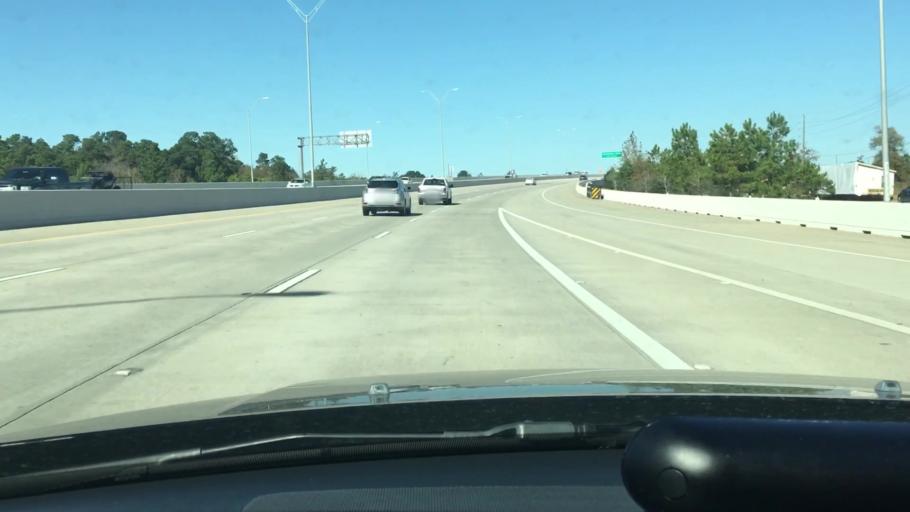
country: US
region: Texas
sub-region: Harris County
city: Sheldon
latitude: 29.8876
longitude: -95.2014
